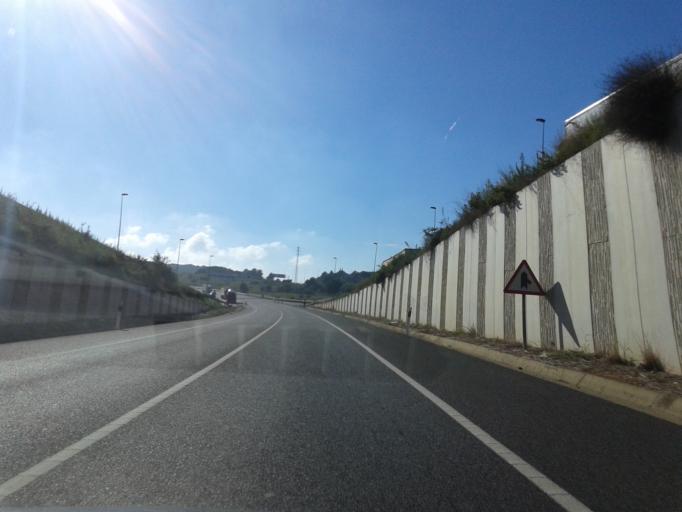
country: ES
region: Catalonia
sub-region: Provincia de Tarragona
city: Torredembarra
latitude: 41.1585
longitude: 1.3912
